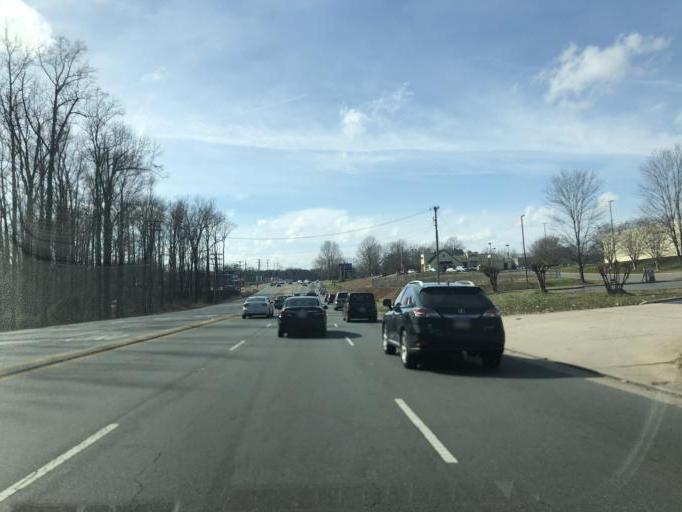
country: US
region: North Carolina
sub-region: Gaston County
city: Lowell
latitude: 35.2579
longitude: -81.1166
